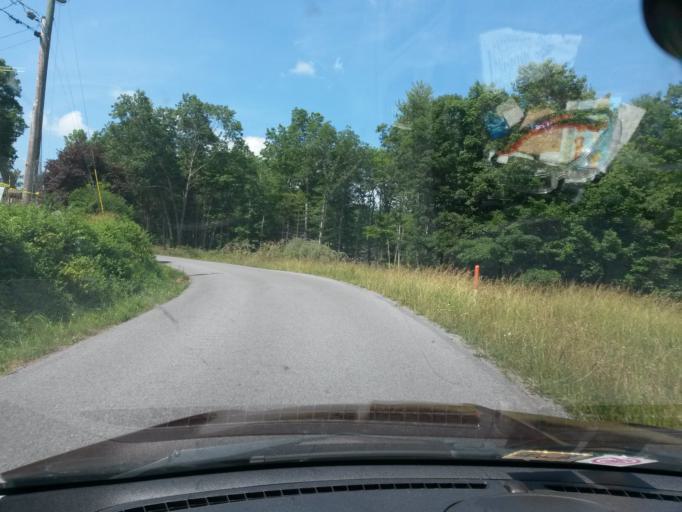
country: US
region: West Virginia
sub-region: Mercer County
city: Princeton
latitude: 37.3959
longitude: -81.1126
